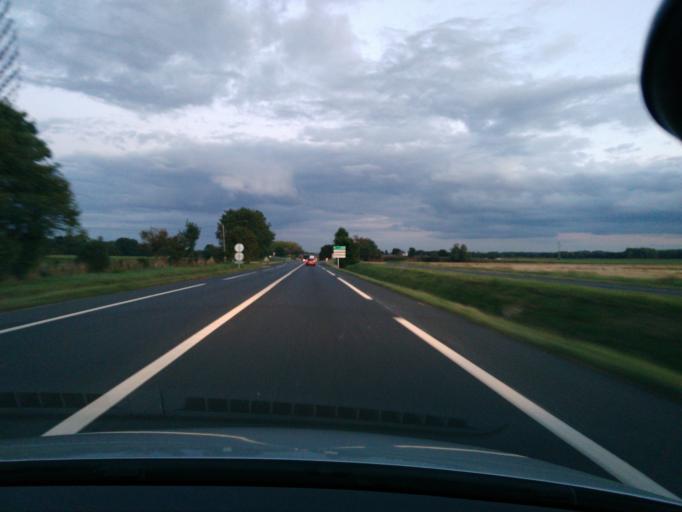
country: FR
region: Ile-de-France
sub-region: Departement de Seine-et-Marne
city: Saint-Germain-sur-Morin
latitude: 48.8586
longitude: 2.8493
